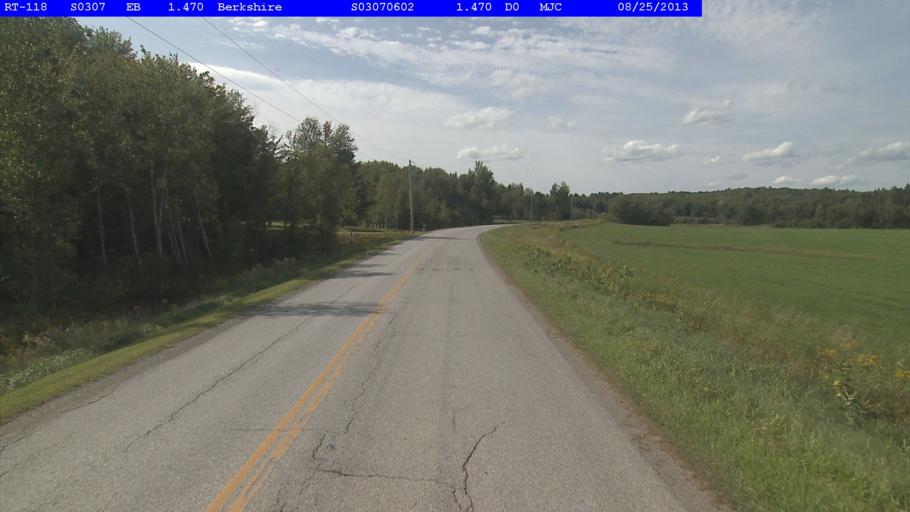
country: US
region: Vermont
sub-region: Franklin County
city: Enosburg Falls
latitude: 44.9415
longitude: -72.7379
